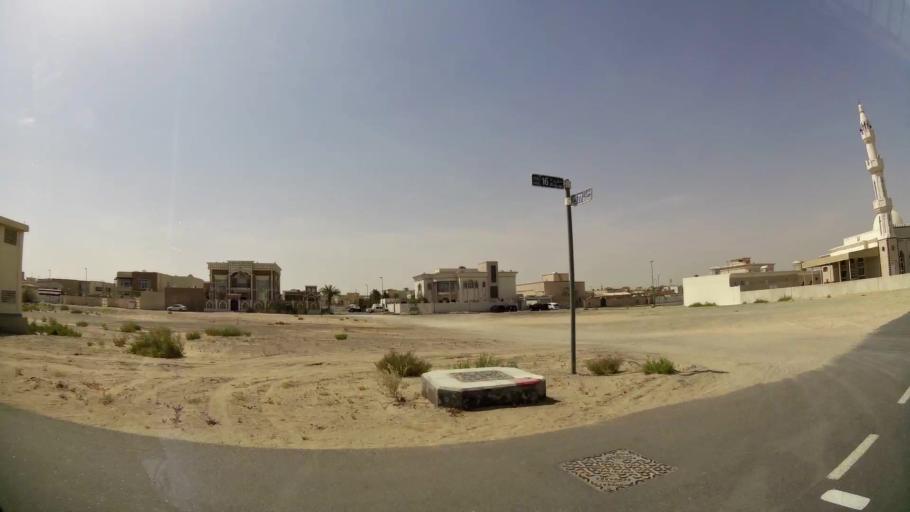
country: AE
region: Ash Shariqah
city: Sharjah
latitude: 25.1955
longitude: 55.4411
